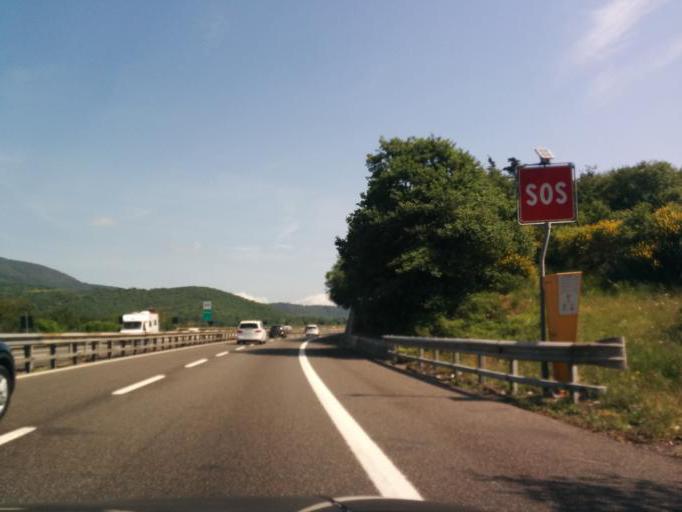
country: IT
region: Tuscany
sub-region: Province of Florence
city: Carraia
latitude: 43.9095
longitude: 11.1949
